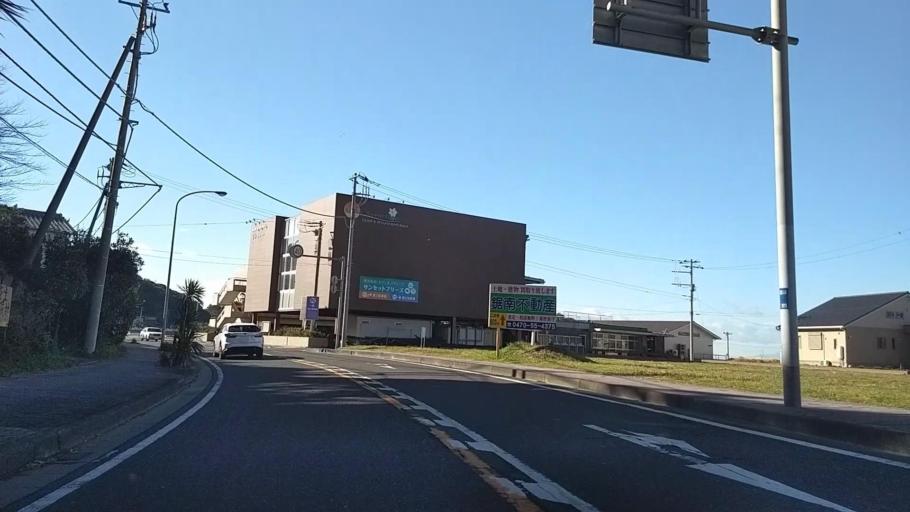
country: JP
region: Chiba
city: Tateyama
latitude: 35.1278
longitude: 139.8373
